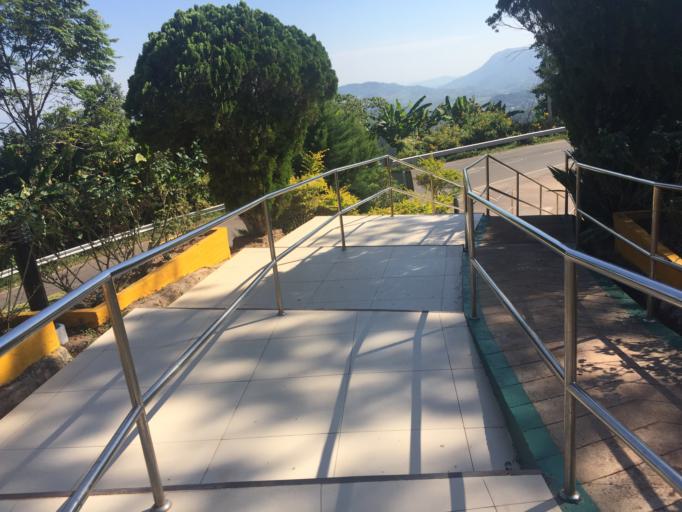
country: TH
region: Phetchabun
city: Khao Kho
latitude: 16.6151
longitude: 100.9858
